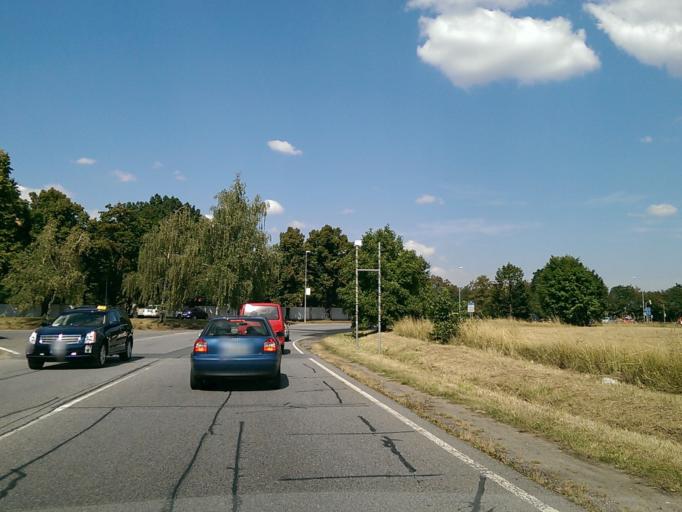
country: CZ
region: Central Bohemia
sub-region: Okres Praha-Zapad
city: Pruhonice
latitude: 50.0351
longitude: 14.5648
